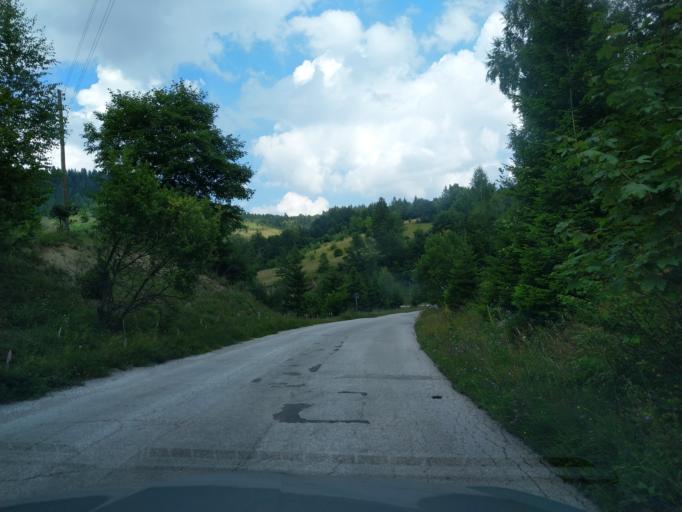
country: RS
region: Central Serbia
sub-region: Zlatiborski Okrug
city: Nova Varos
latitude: 43.5370
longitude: 19.9063
